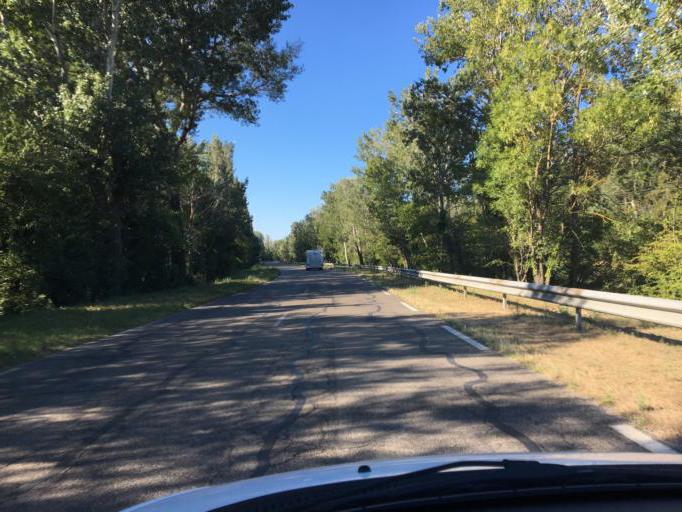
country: FR
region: Languedoc-Roussillon
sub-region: Departement du Gard
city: Villeneuve-les-Avignon
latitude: 43.9695
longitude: 4.8191
